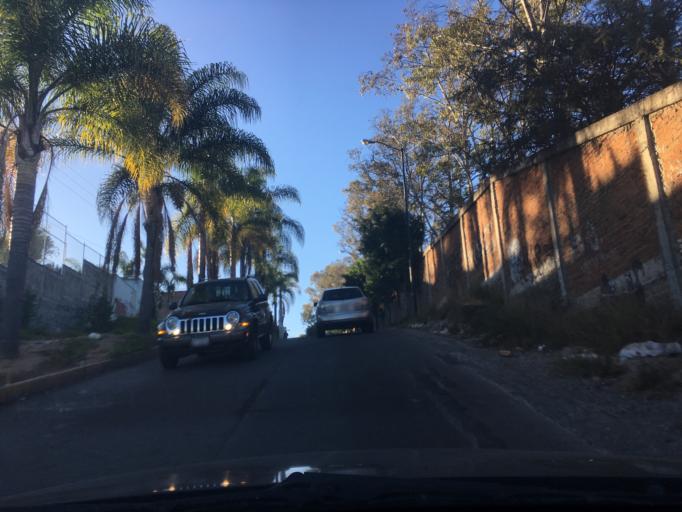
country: MX
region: Michoacan
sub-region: Morelia
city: Montana Monarca (Punta Altozano)
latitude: 19.6661
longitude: -101.2012
